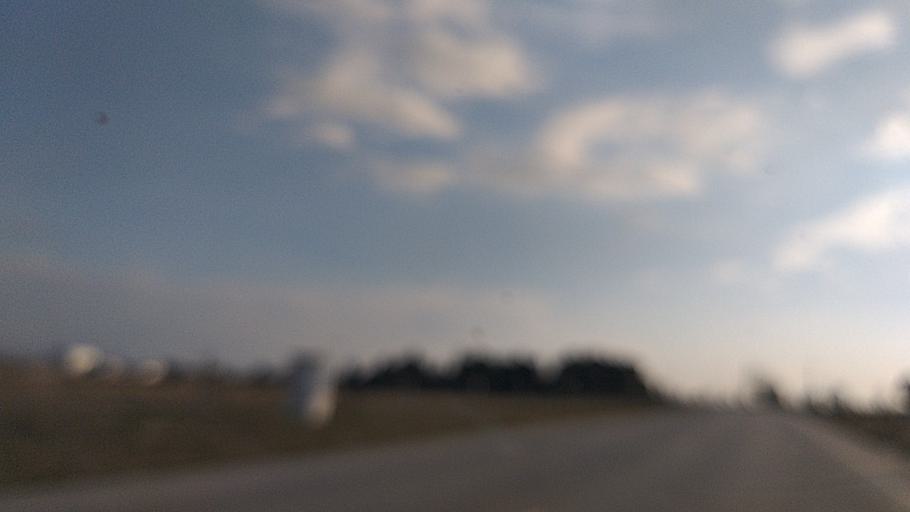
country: ES
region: Castille and Leon
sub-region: Provincia de Salamanca
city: Fuentes de Onoro
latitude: 40.5983
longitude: -6.9911
